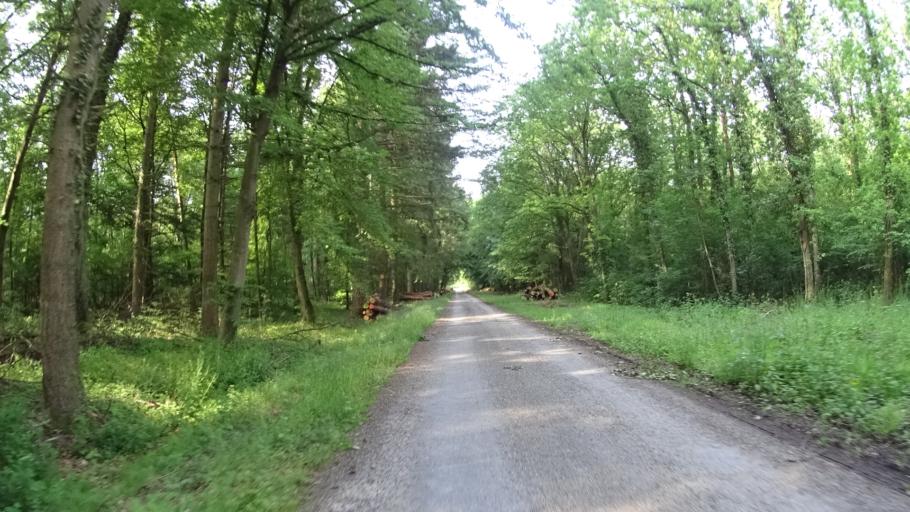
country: DE
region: Baden-Wuerttemberg
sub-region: Karlsruhe Region
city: Sandhausen
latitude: 49.3365
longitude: 8.6258
